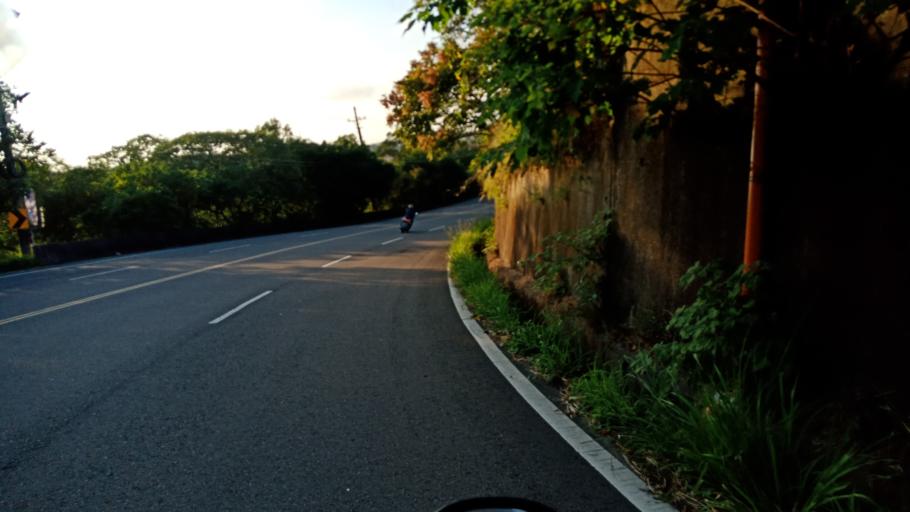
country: TW
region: Taiwan
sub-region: Hsinchu
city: Hsinchu
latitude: 24.7606
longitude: 120.9964
